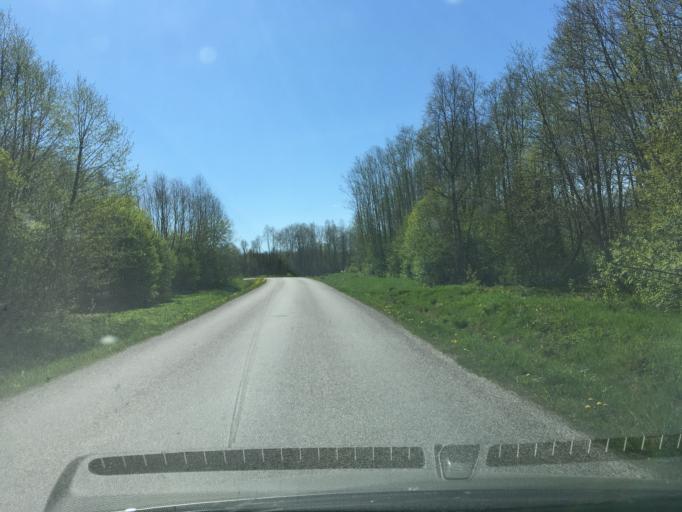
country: EE
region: Harju
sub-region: Raasiku vald
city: Arukula
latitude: 59.4048
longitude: 25.0777
